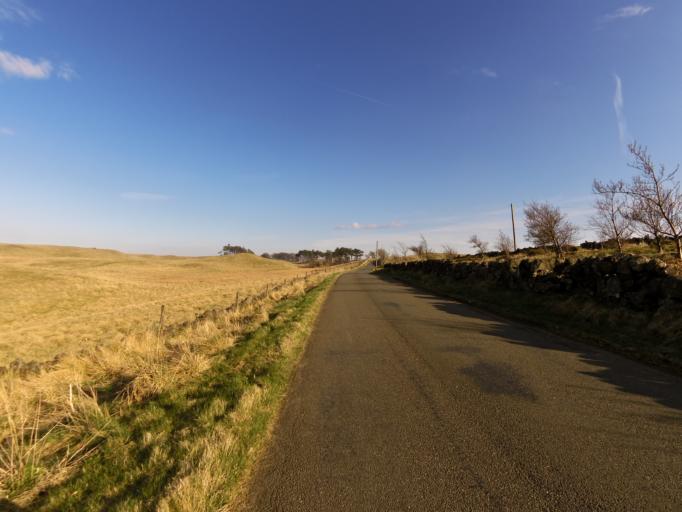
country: GB
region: Scotland
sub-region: Fife
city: Falkland
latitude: 56.2382
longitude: -3.2462
